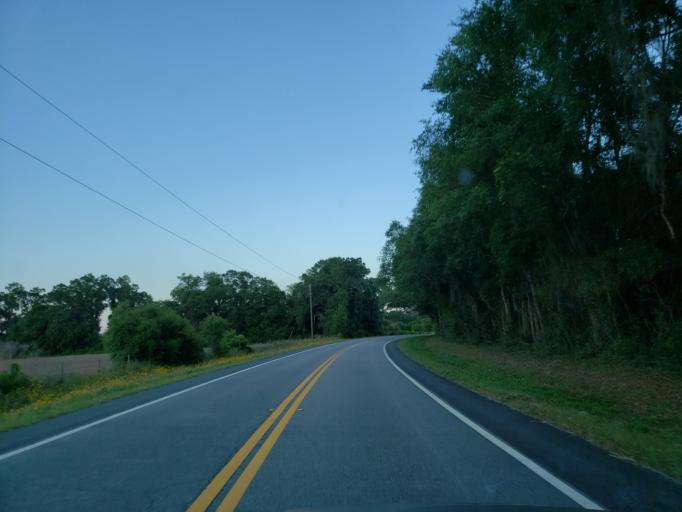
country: US
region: Georgia
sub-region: Echols County
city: Statenville
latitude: 30.5586
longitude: -83.1295
